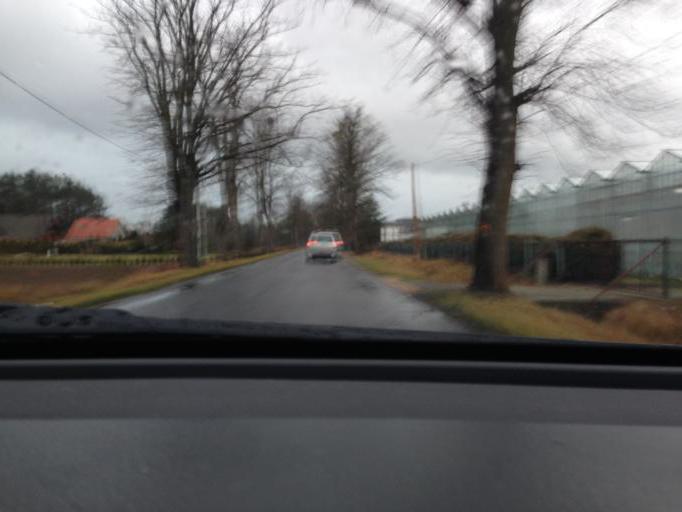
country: PL
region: Opole Voivodeship
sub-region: Powiat opolski
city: Wegry
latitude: 50.7246
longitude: 18.0253
